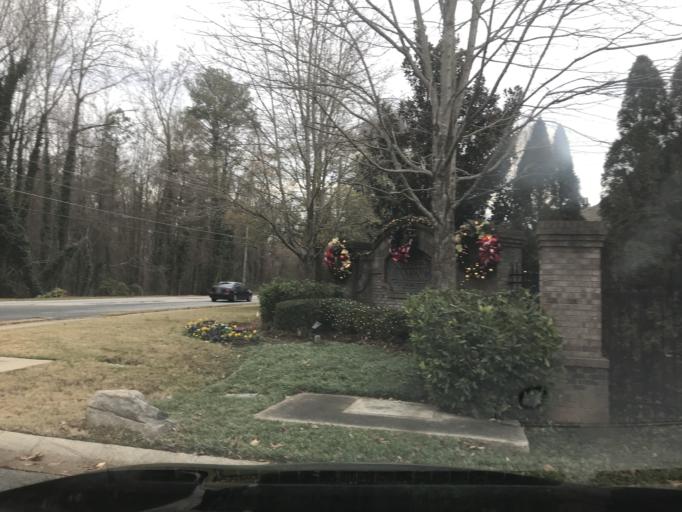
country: US
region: Georgia
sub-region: Fulton County
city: East Point
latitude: 33.7147
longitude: -84.5070
